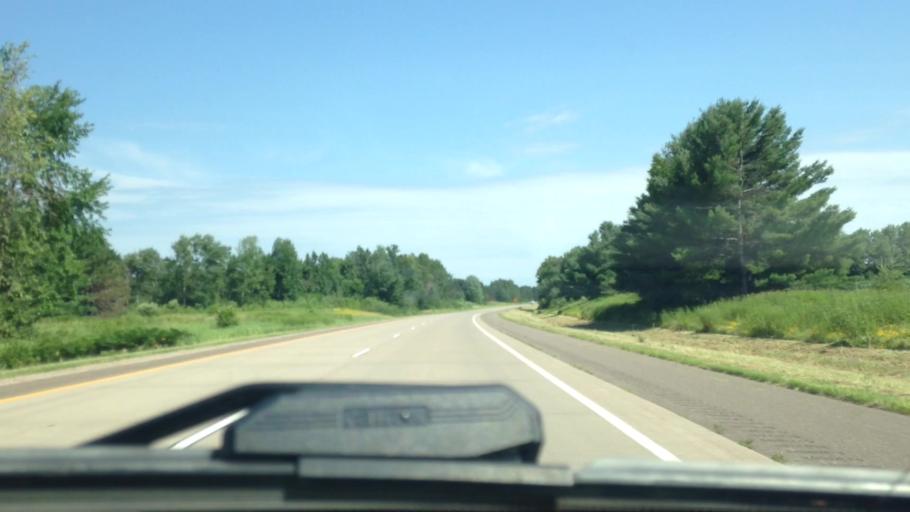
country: US
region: Wisconsin
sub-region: Barron County
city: Rice Lake
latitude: 45.5561
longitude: -91.7652
